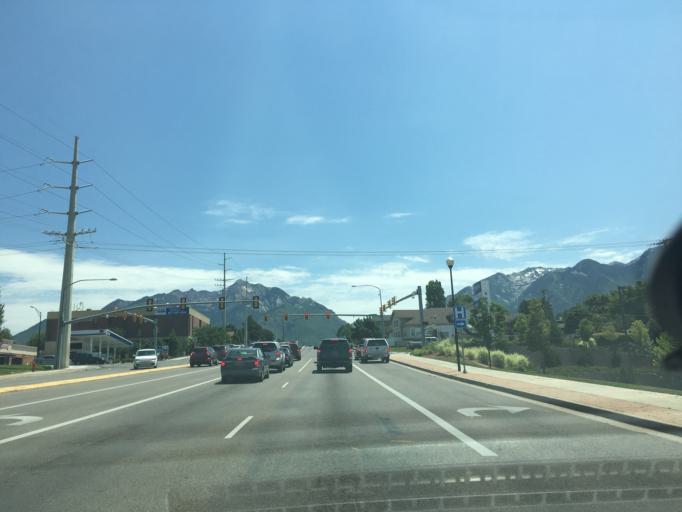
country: US
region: Utah
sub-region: Salt Lake County
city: Sandy Hills
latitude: 40.5804
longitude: -111.8543
